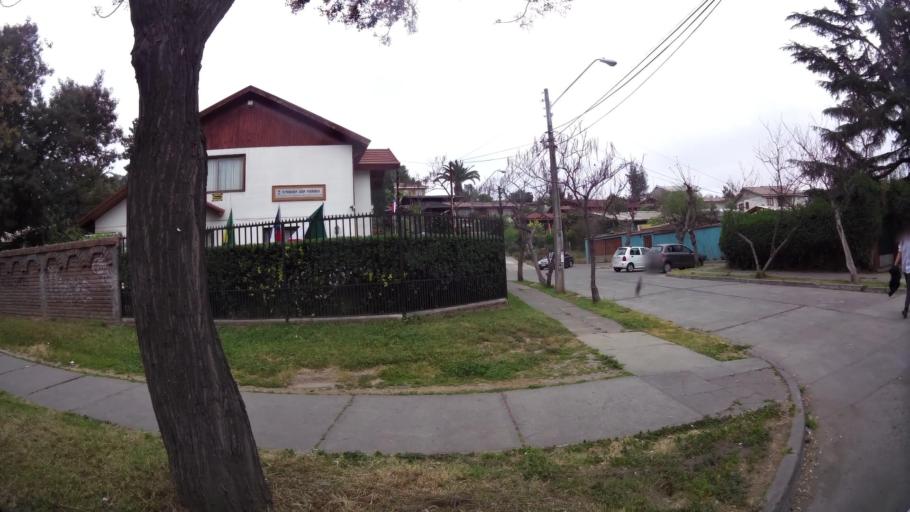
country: CL
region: Santiago Metropolitan
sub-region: Provincia de Santiago
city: Lo Prado
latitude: -33.5014
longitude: -70.7595
